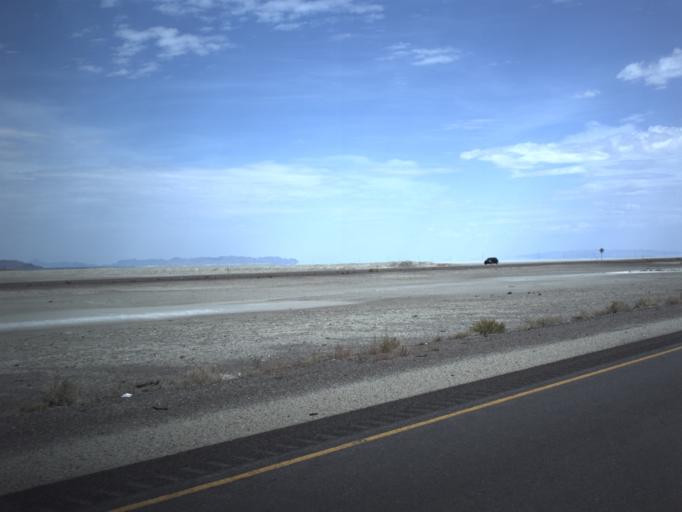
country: US
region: Utah
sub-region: Tooele County
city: Wendover
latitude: 40.7373
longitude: -113.7920
